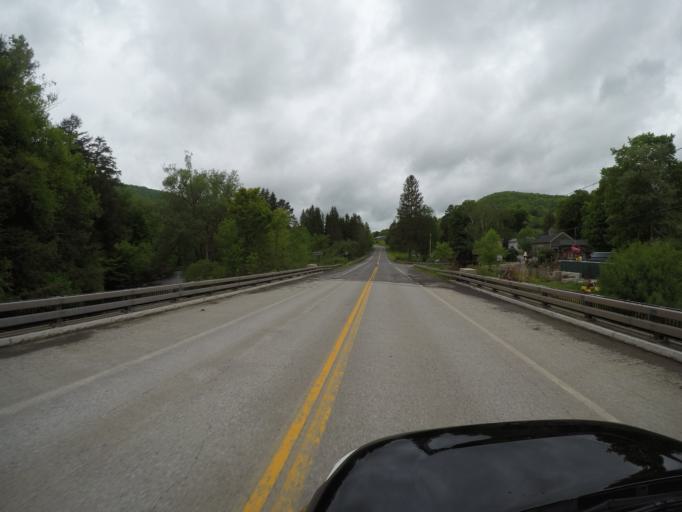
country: US
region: New York
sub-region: Delaware County
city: Delhi
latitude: 42.2486
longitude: -74.8304
